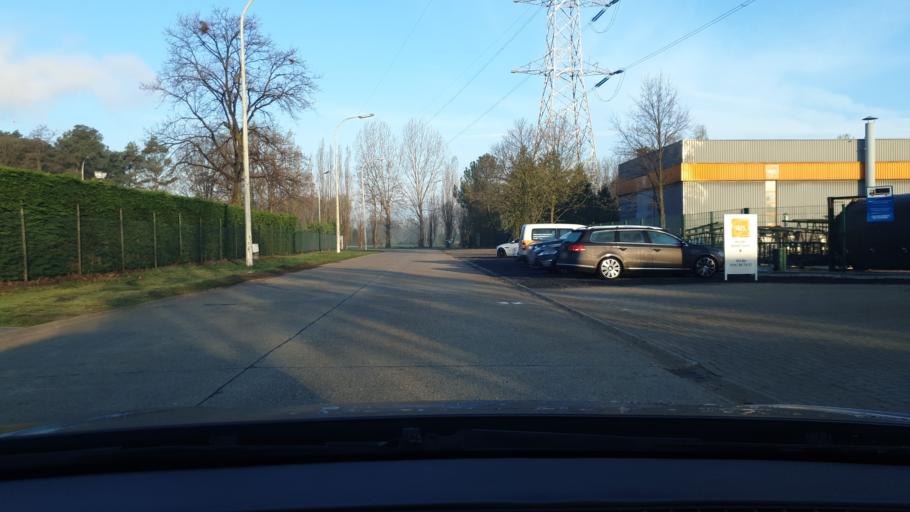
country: BE
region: Flanders
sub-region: Provincie Antwerpen
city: Laakdal
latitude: 51.1193
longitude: 5.0148
